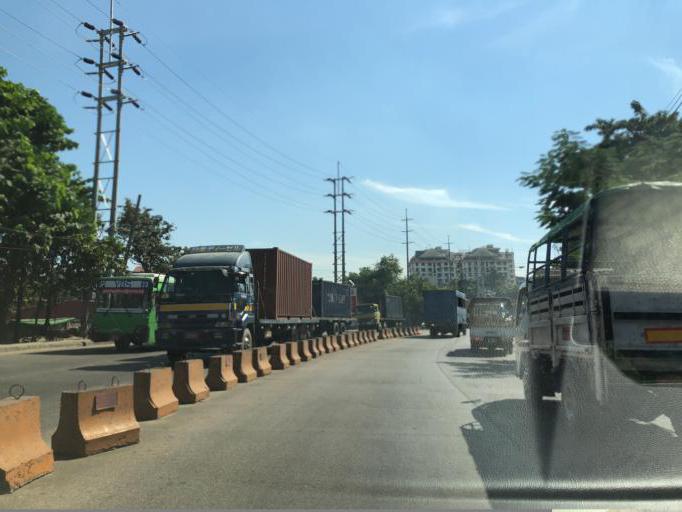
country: MM
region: Yangon
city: Yangon
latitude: 16.8261
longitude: 96.1230
